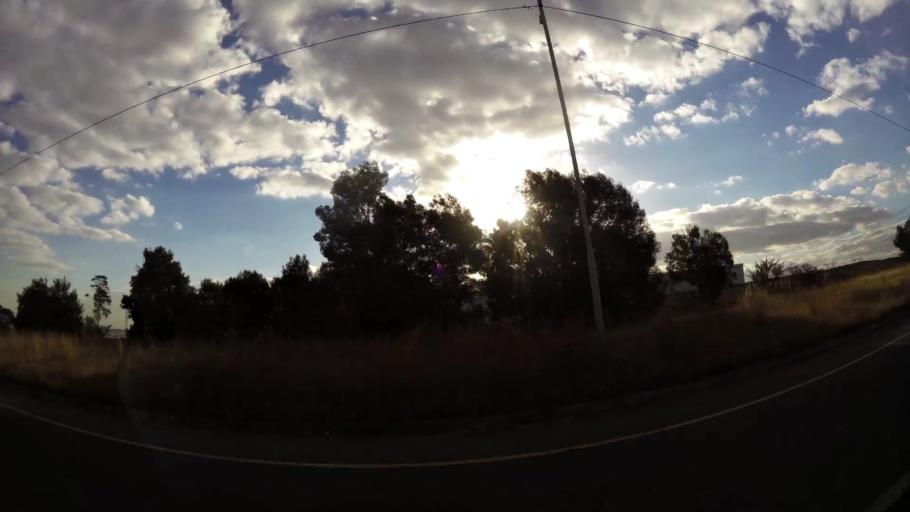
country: ZA
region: Gauteng
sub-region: City of Johannesburg Metropolitan Municipality
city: Midrand
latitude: -25.9266
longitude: 28.1574
